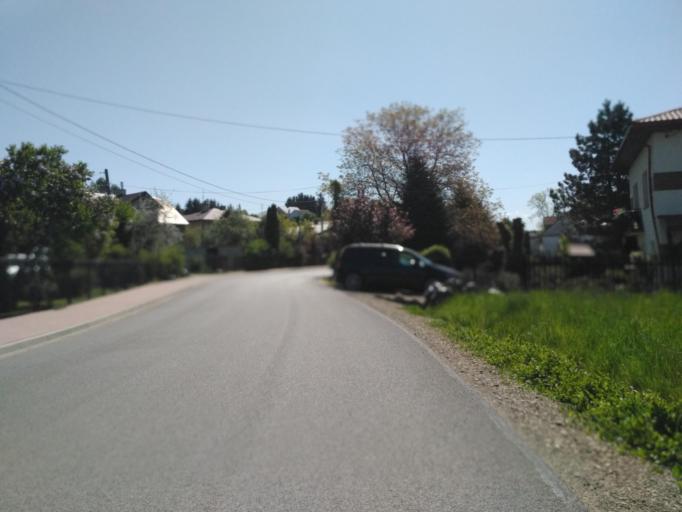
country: PL
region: Subcarpathian Voivodeship
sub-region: Powiat krosnienski
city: Miejsce Piastowe
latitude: 49.6472
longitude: 21.8056
